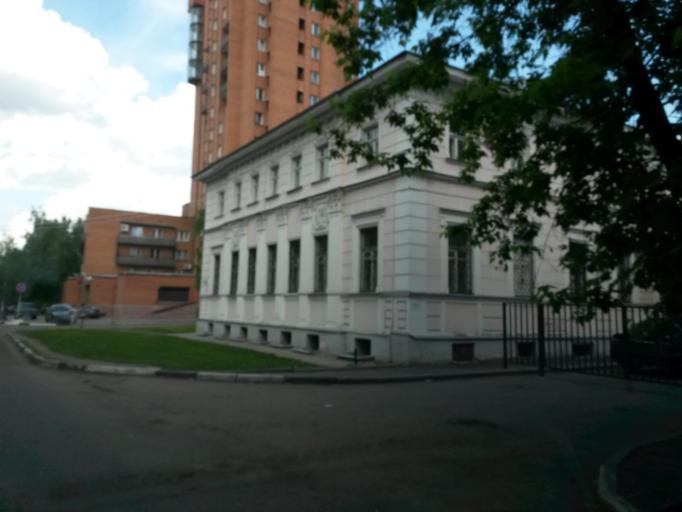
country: RU
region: Jaroslavl
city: Yaroslavl
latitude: 57.6230
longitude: 39.8772
